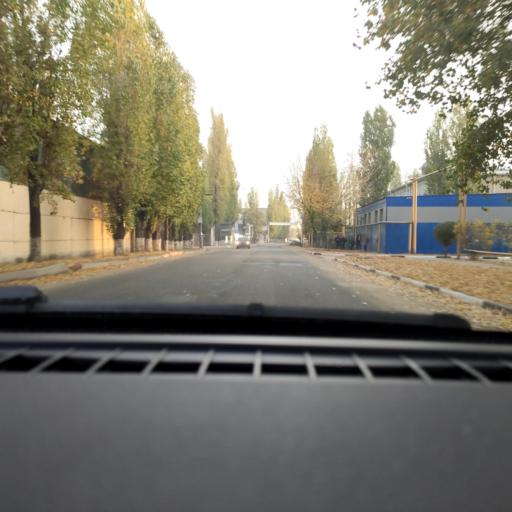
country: RU
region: Voronezj
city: Voronezh
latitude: 51.6519
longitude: 39.2809
